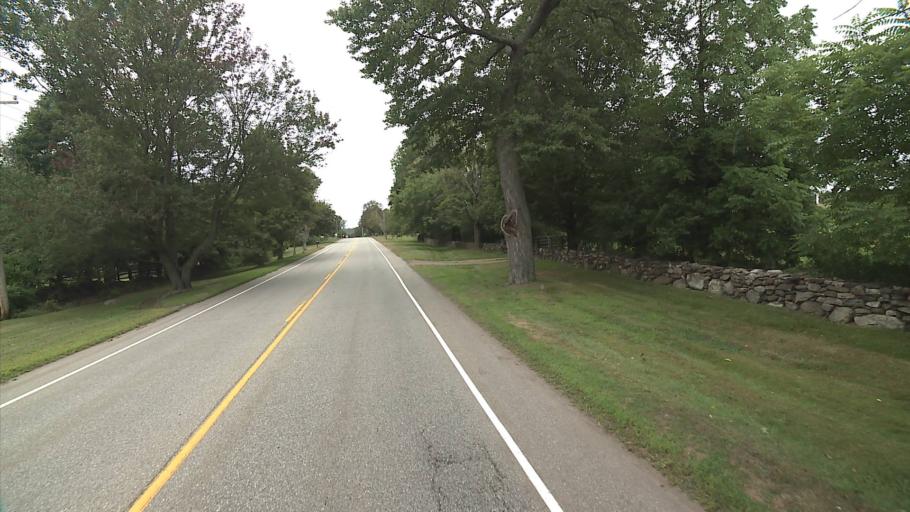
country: US
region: Connecticut
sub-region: Tolland County
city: Hebron
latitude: 41.6834
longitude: -72.4161
